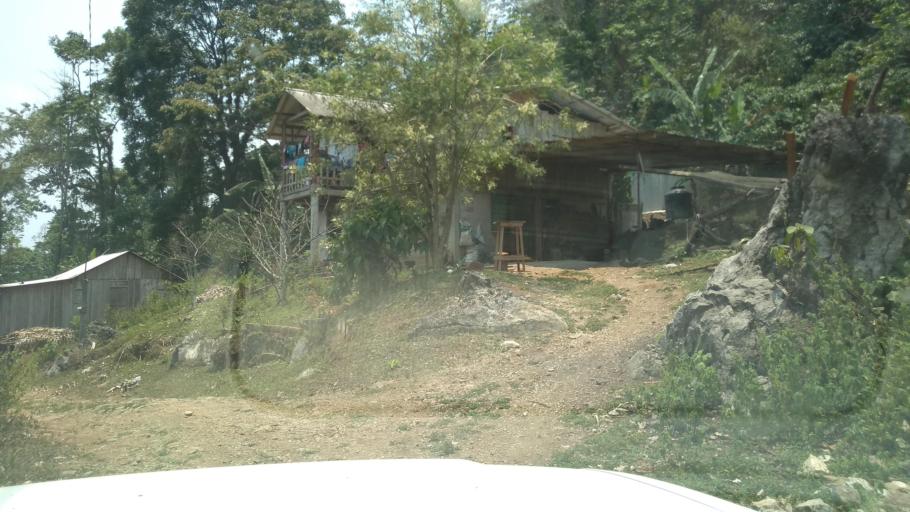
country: MX
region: Veracruz
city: Motzorongo
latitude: 18.6040
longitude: -96.7537
